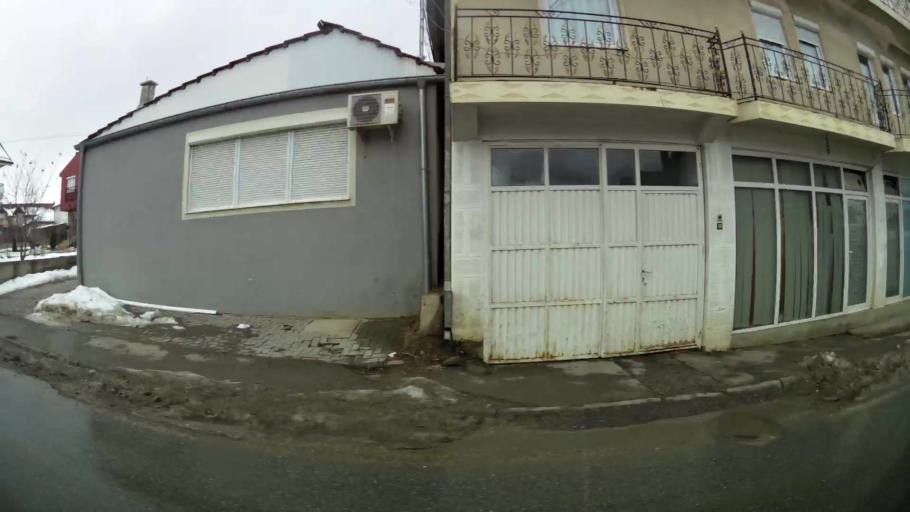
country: XK
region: Pristina
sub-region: Komuna e Prishtines
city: Pristina
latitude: 42.6616
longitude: 21.1816
